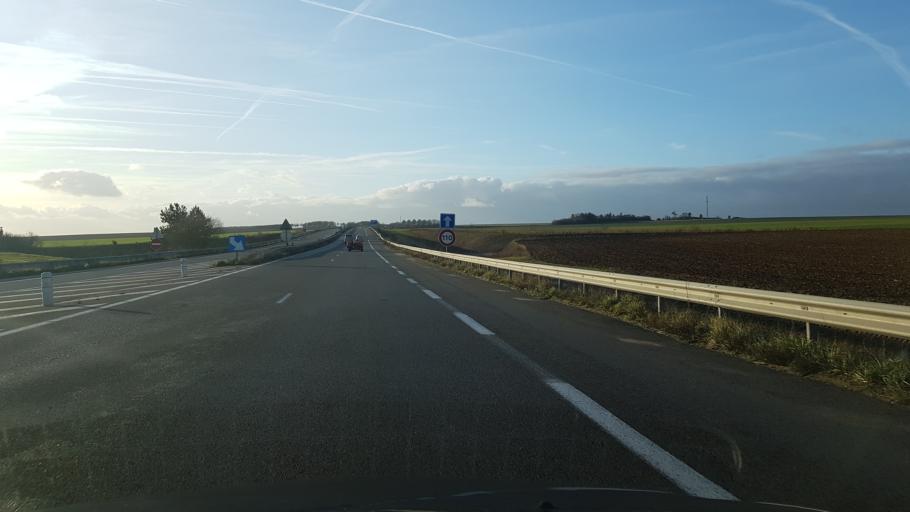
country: FR
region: Champagne-Ardenne
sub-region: Departement de l'Aube
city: Mailly-le-Camp
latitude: 48.7322
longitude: 4.2542
